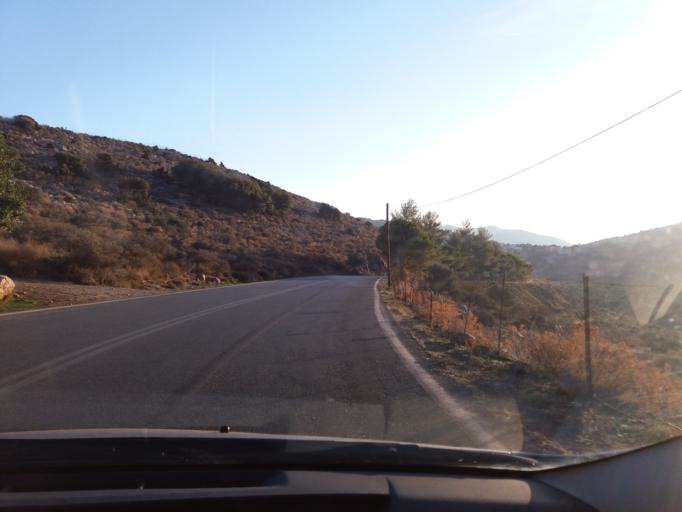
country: GR
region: Crete
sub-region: Nomos Irakleiou
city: Mokhos
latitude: 35.2717
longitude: 25.4270
